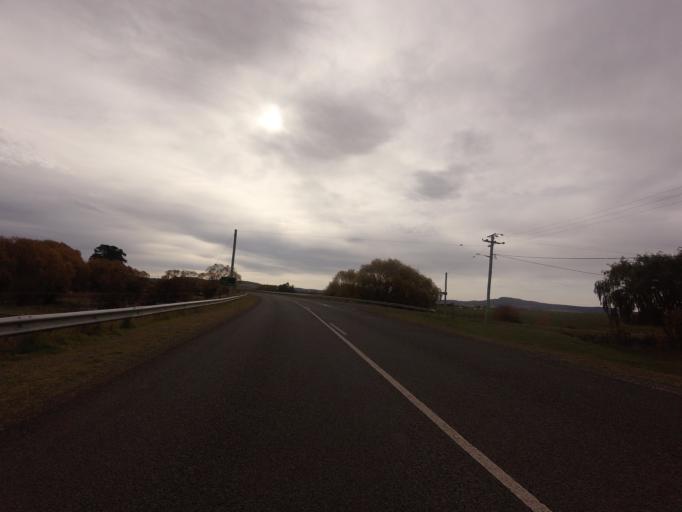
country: AU
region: Tasmania
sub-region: Derwent Valley
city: New Norfolk
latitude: -42.3806
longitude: 147.0034
